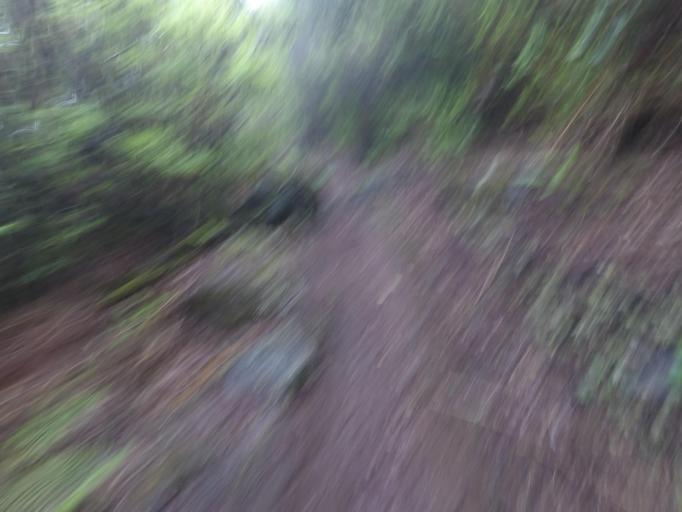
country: PT
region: Madeira
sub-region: Calheta
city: Arco da Calheta
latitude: 32.7699
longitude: -17.1176
